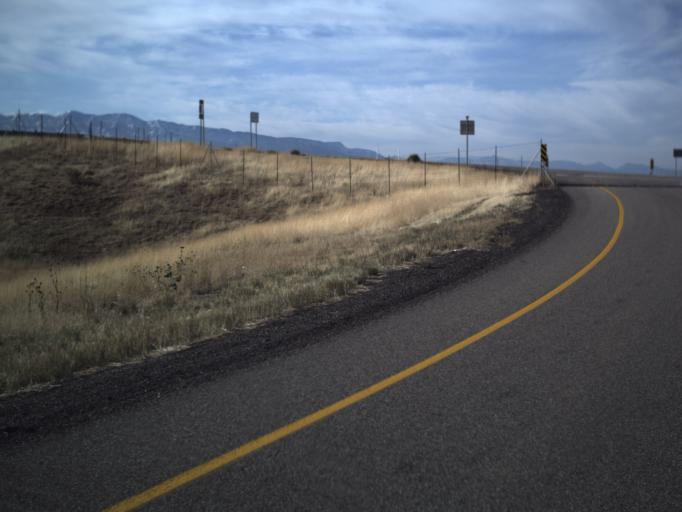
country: US
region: Utah
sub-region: Millard County
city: Fillmore
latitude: 39.1455
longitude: -112.2368
